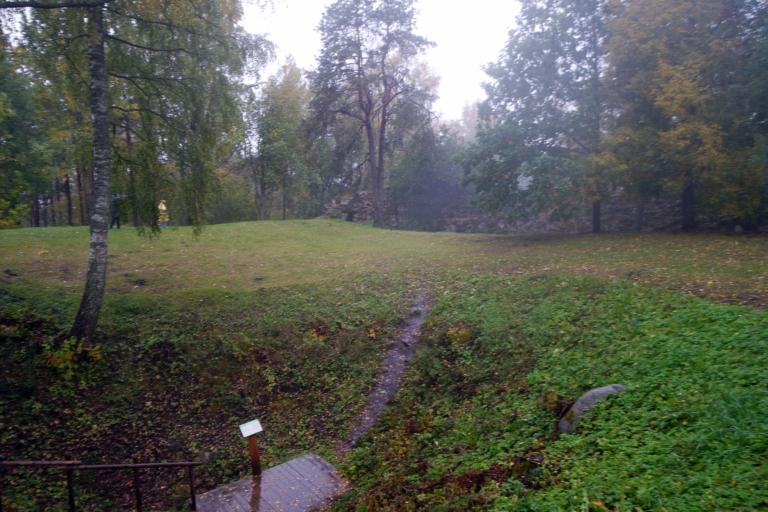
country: LV
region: Dagda
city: Dagda
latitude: 56.2778
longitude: 27.4134
